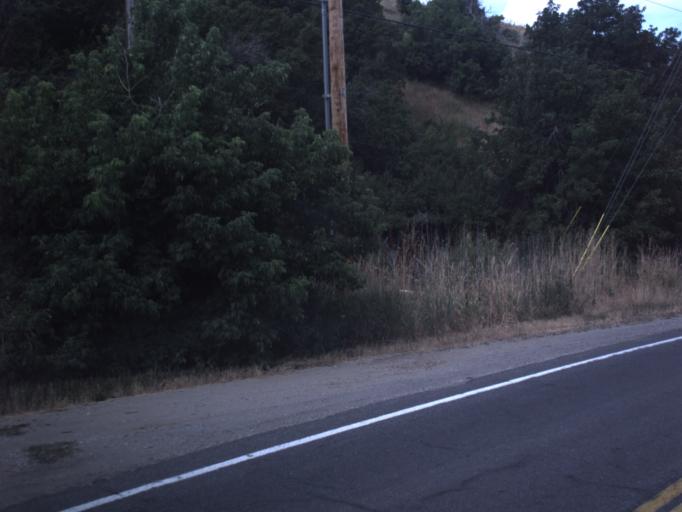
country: US
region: Utah
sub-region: Davis County
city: Hill Air Force Bace
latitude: 41.1392
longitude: -111.9683
